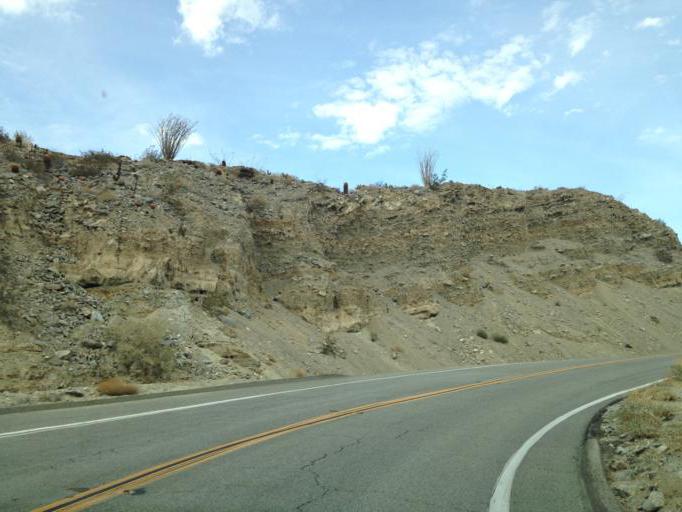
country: US
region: California
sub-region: San Diego County
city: Borrego Springs
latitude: 33.1403
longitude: -116.3690
